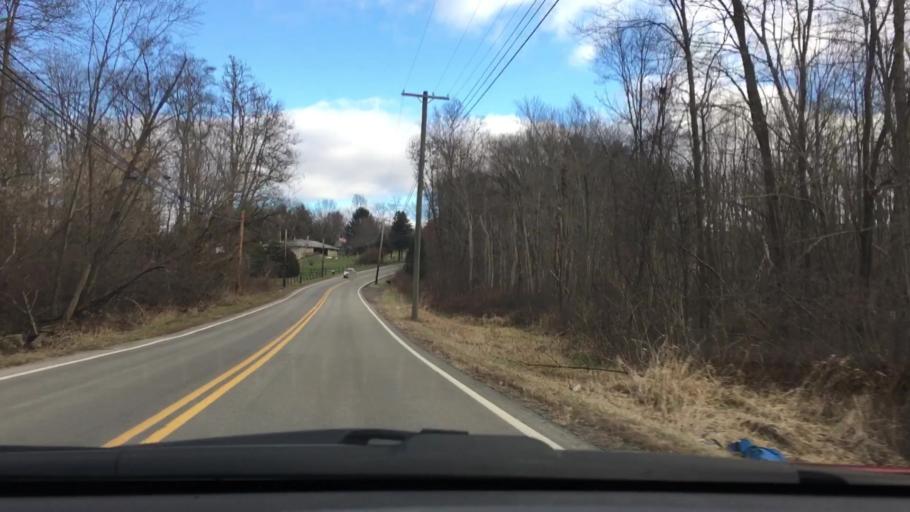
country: US
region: Pennsylvania
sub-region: Armstrong County
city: Orchard Hills
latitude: 40.6038
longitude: -79.5010
